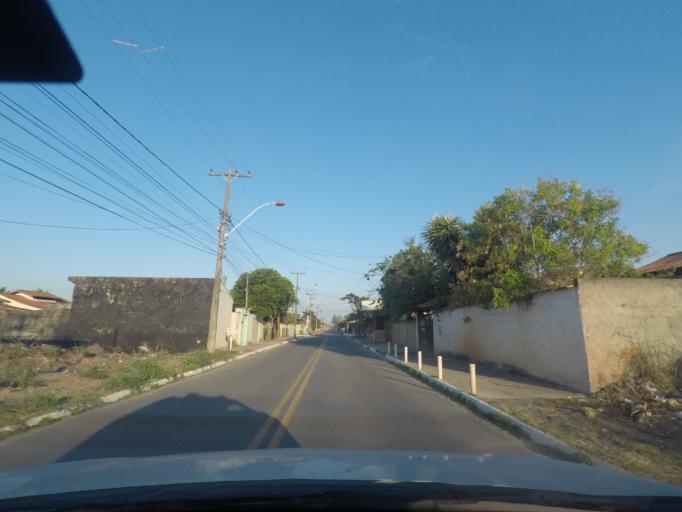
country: BR
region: Rio de Janeiro
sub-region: Marica
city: Marica
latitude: -22.9670
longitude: -42.9305
